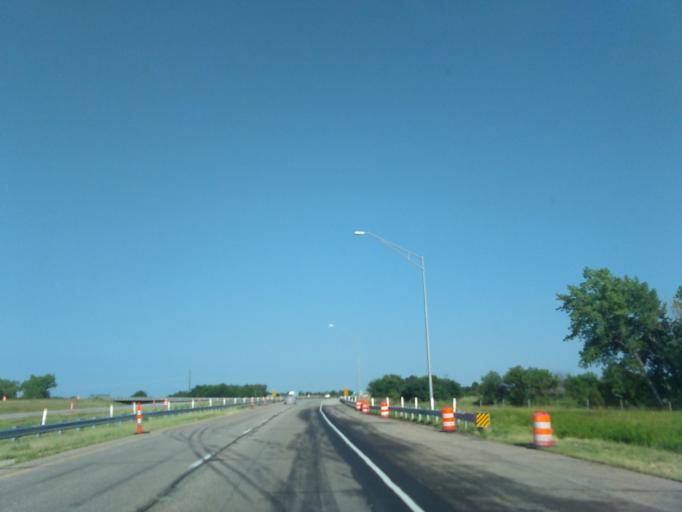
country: US
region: Nebraska
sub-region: Hall County
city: Grand Island
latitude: 40.8254
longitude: -98.3372
